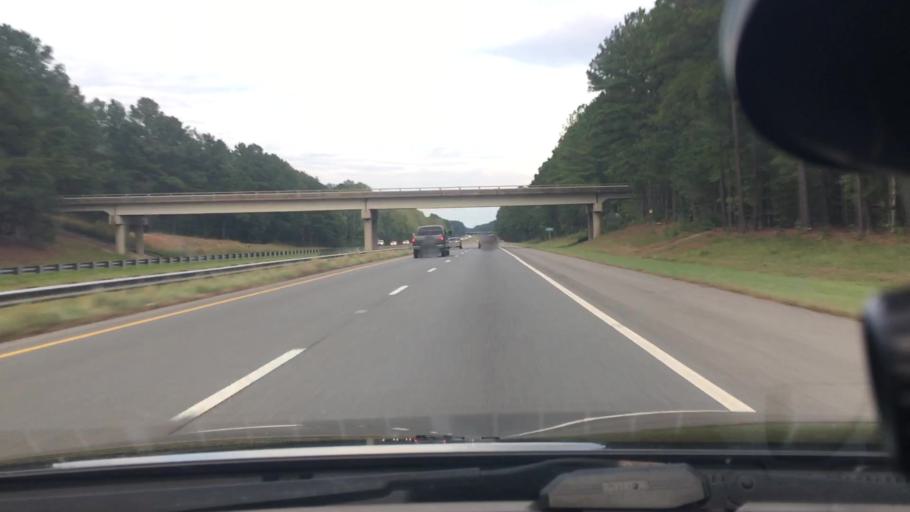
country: US
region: North Carolina
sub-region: Chatham County
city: Farmville
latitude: 35.5768
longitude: -79.1360
